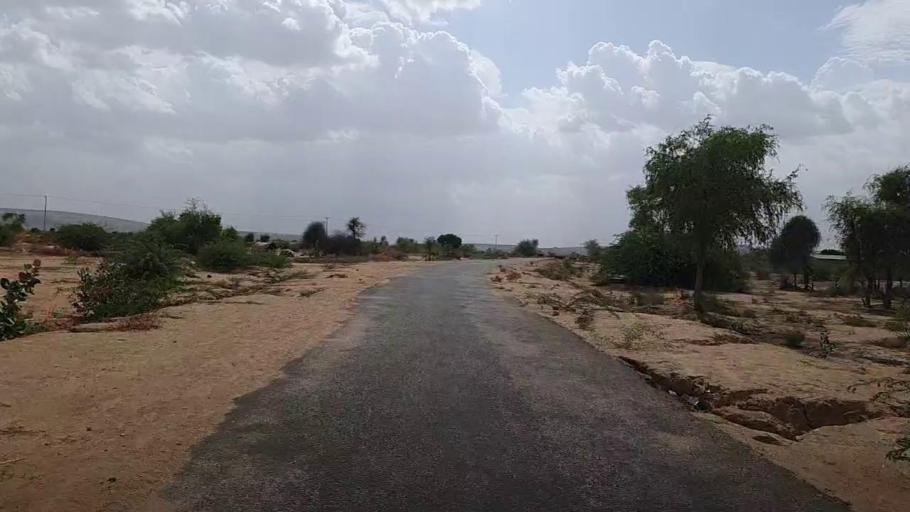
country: PK
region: Sindh
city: Jamshoro
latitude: 25.4034
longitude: 67.7825
